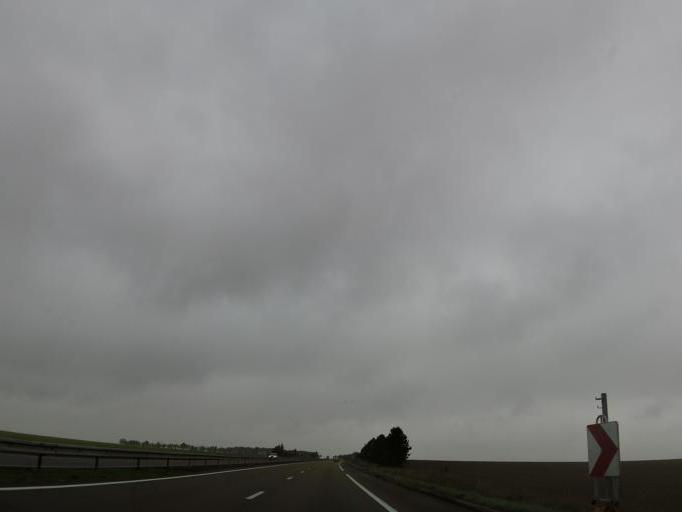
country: FR
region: Champagne-Ardenne
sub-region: Departement de la Marne
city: Verzy
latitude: 49.1033
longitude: 4.2546
